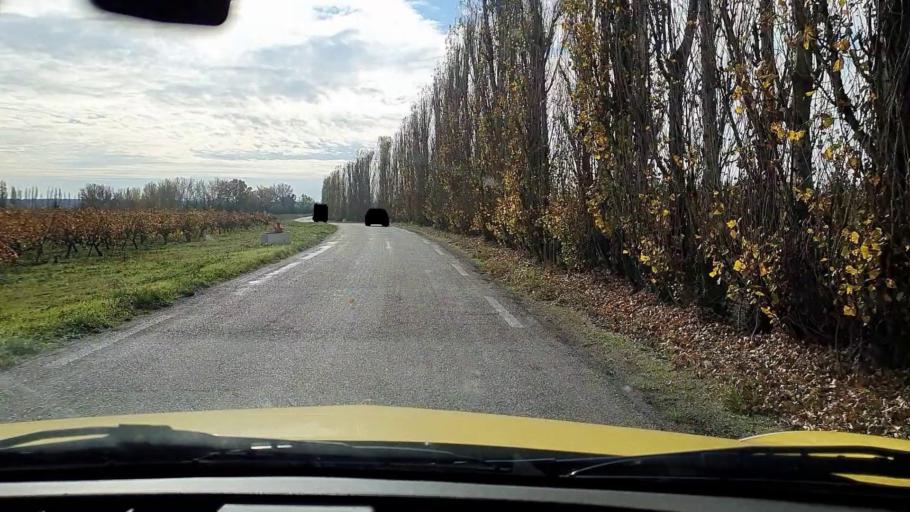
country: FR
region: Languedoc-Roussillon
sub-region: Departement du Gard
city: Jonquieres-Saint-Vincent
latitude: 43.8413
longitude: 4.5696
